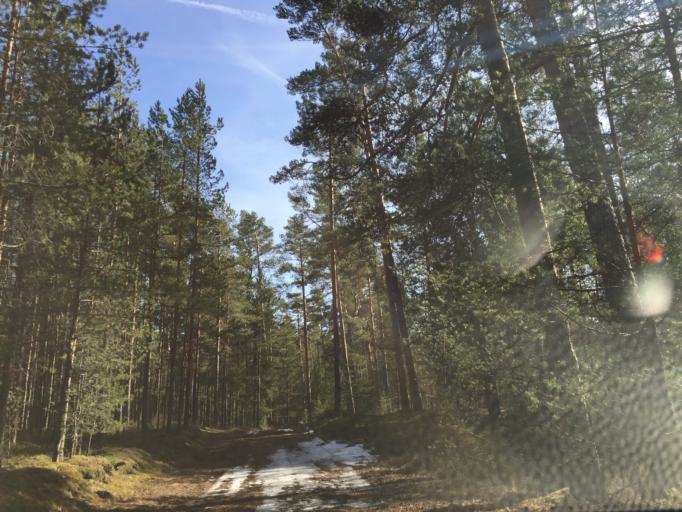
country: EE
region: Paernumaa
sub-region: Paernu linn
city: Parnu
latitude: 58.2318
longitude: 24.5178
